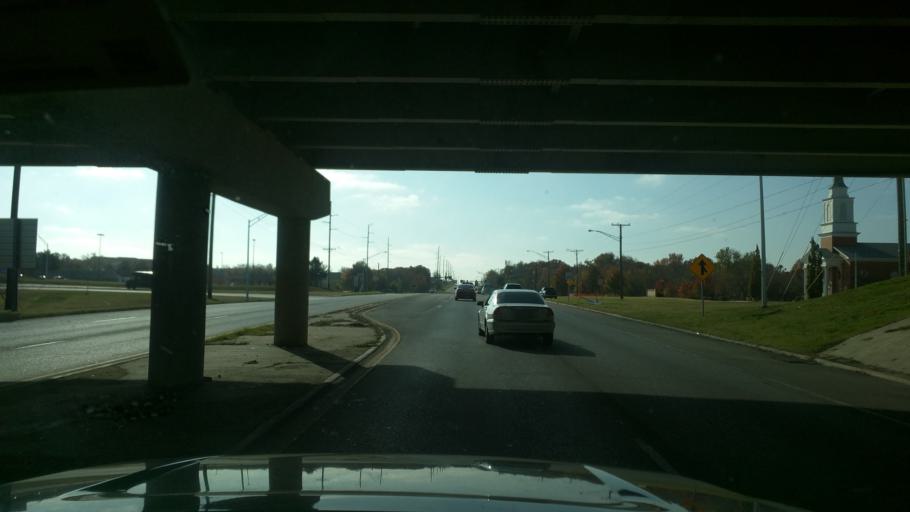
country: US
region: Oklahoma
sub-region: Washington County
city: Bartlesville
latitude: 36.7427
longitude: -95.9354
